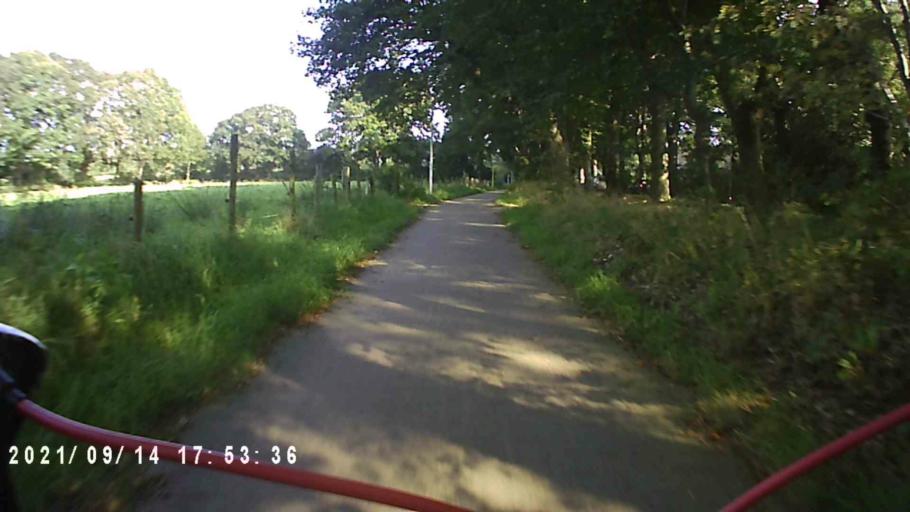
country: NL
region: Groningen
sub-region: Gemeente Haren
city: Haren
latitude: 53.1310
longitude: 6.6359
